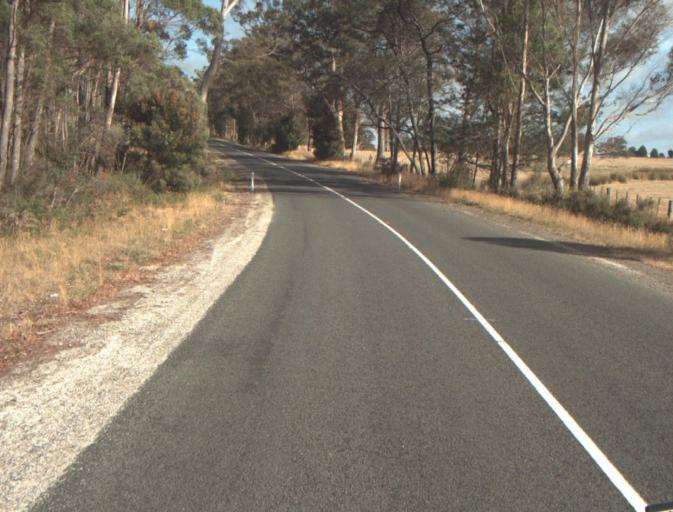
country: AU
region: Tasmania
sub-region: Dorset
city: Bridport
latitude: -41.1168
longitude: 147.2045
